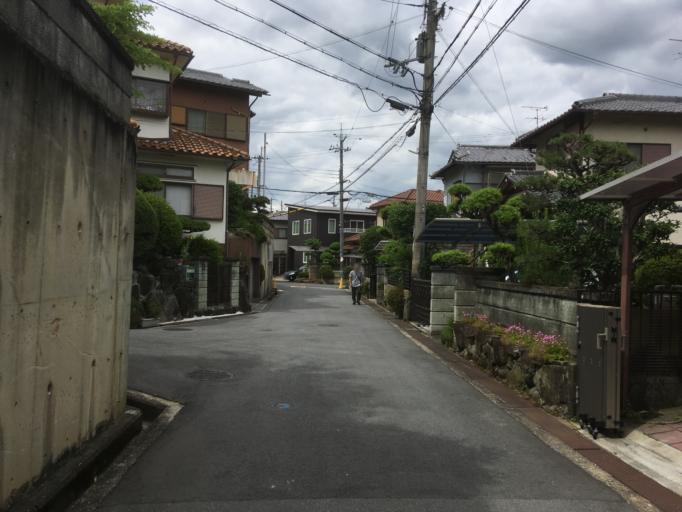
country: JP
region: Nara
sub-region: Ikoma-shi
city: Ikoma
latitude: 34.6741
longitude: 135.7018
